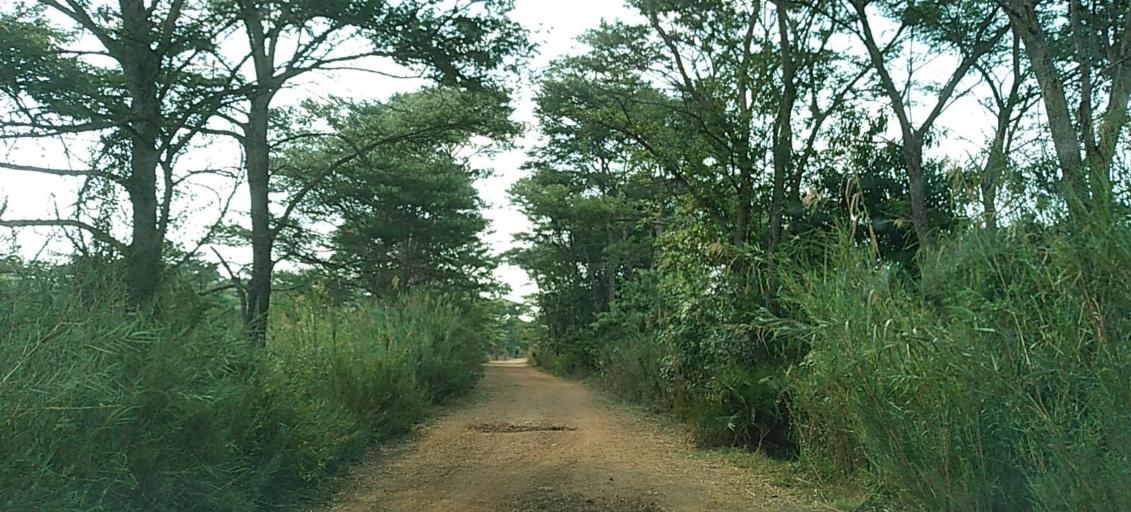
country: ZM
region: Copperbelt
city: Mpongwe
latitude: -13.4754
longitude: 28.0773
